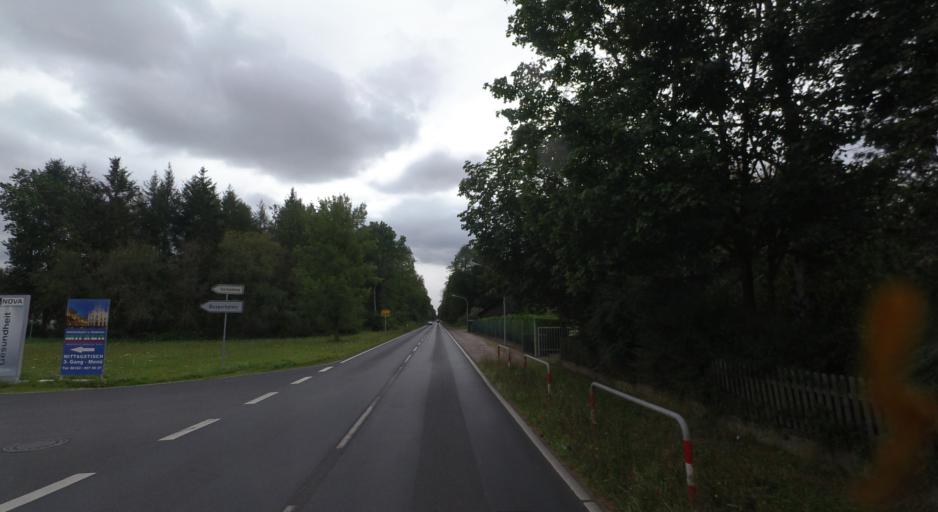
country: DE
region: Hesse
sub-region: Regierungsbezirk Darmstadt
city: Seligenstadt
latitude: 50.0331
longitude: 8.9848
